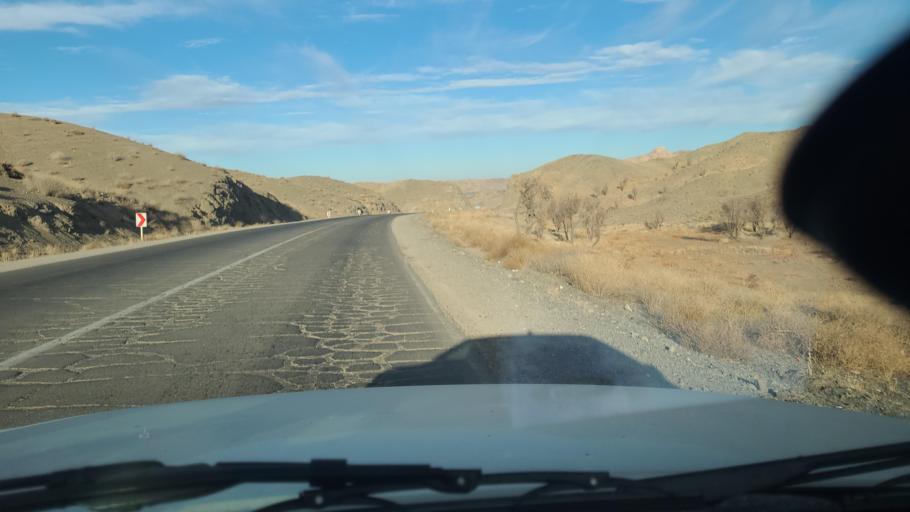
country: IR
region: Razavi Khorasan
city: Sabzevar
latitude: 36.4157
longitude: 57.5522
